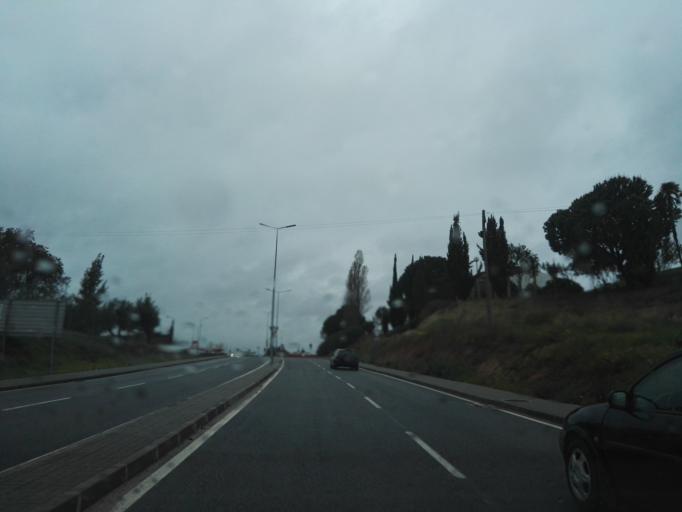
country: PT
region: Portalegre
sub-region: Portalegre
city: Portalegre
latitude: 39.2759
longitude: -7.4273
